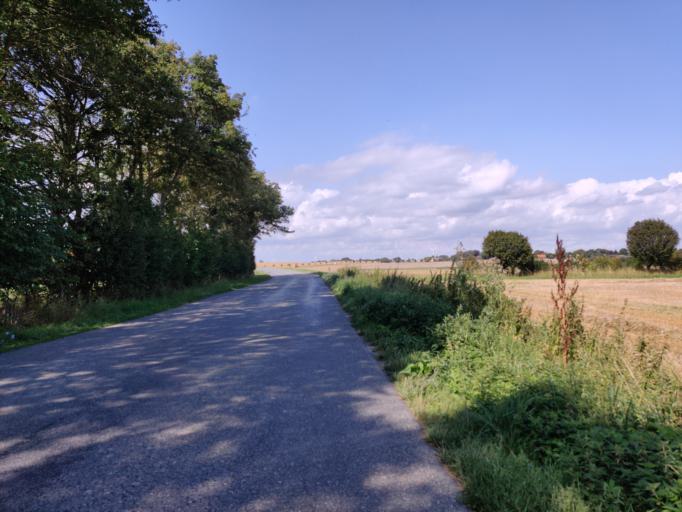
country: DK
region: Zealand
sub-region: Guldborgsund Kommune
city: Nykobing Falster
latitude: 54.6454
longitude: 11.8923
